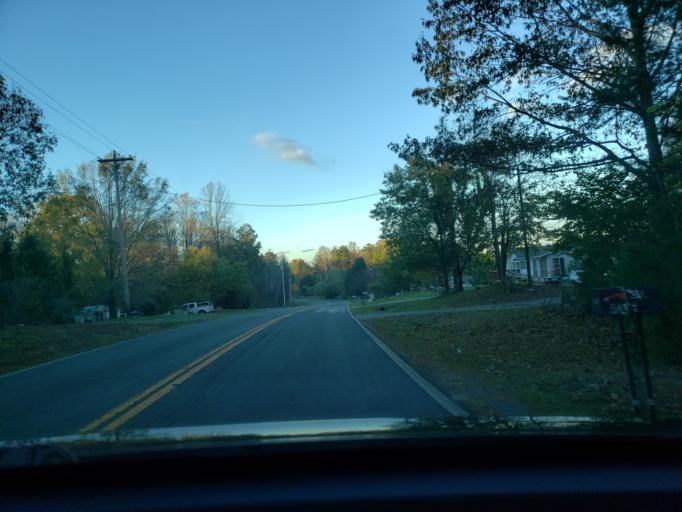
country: US
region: North Carolina
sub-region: Stokes County
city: Danbury
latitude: 36.3721
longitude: -80.1896
